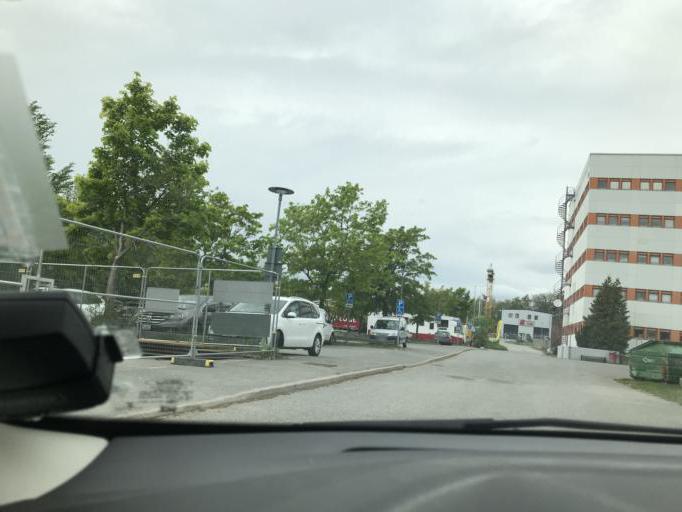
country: SE
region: Stockholm
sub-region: Botkyrka Kommun
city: Alby
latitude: 59.2341
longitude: 17.8353
